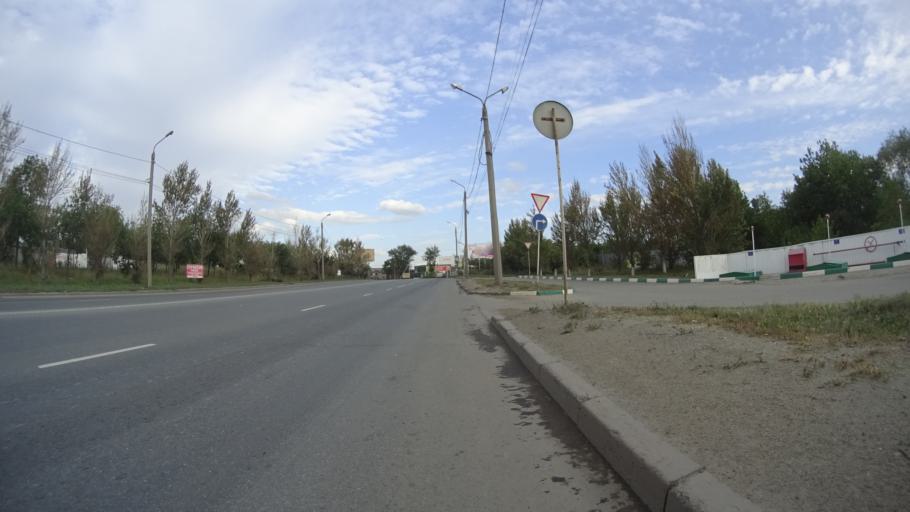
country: RU
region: Chelyabinsk
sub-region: Gorod Chelyabinsk
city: Chelyabinsk
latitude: 55.1924
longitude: 61.4220
